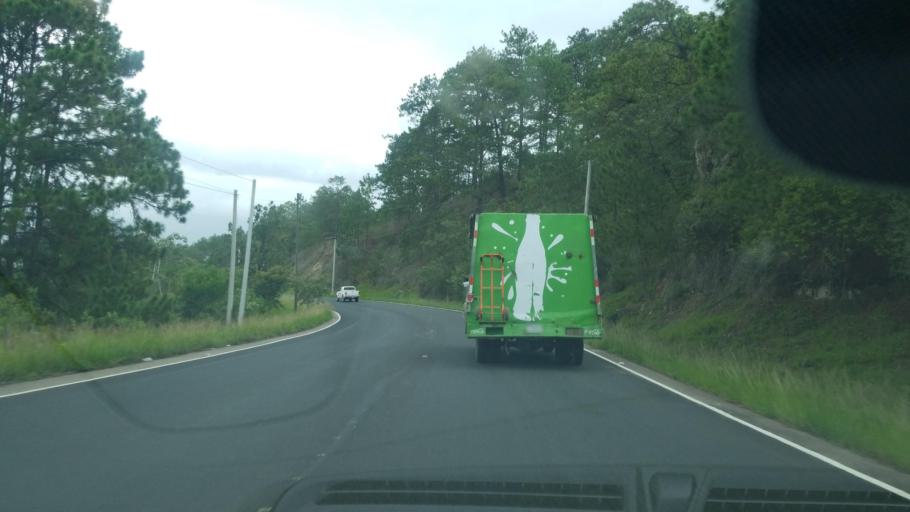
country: HN
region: Ocotepeque
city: Sinuapa
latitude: 14.4559
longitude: -89.1487
